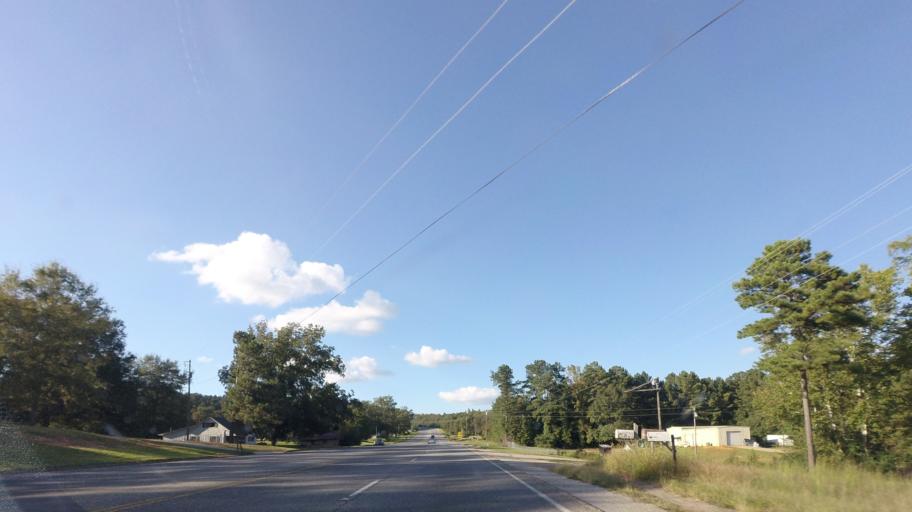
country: US
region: Georgia
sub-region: Pike County
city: Zebulon
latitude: 33.0202
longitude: -84.3244
